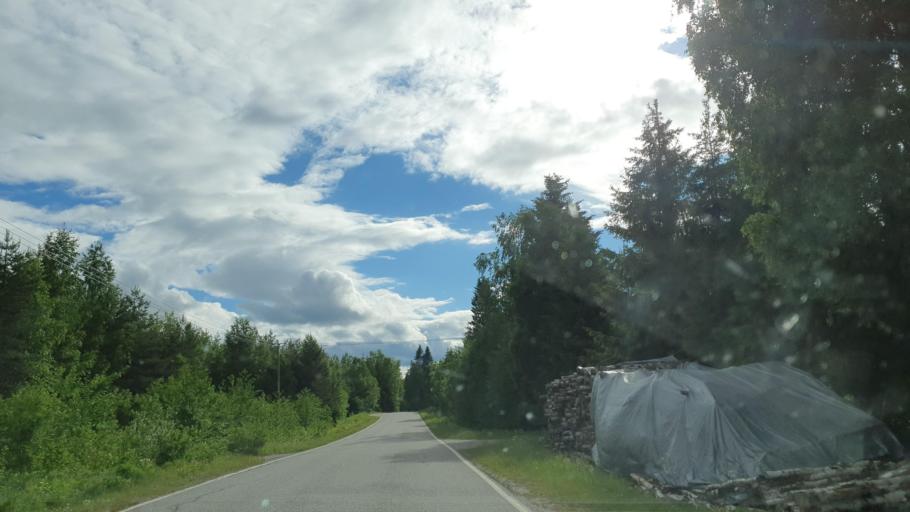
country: FI
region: Kainuu
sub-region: Kajaani
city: Ristijaervi
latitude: 64.3375
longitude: 28.0765
